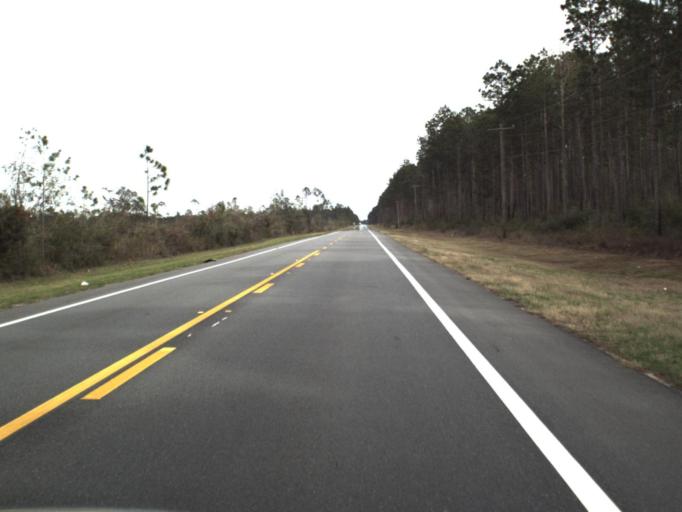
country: US
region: Florida
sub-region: Bay County
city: Callaway
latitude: 30.1401
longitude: -85.4017
